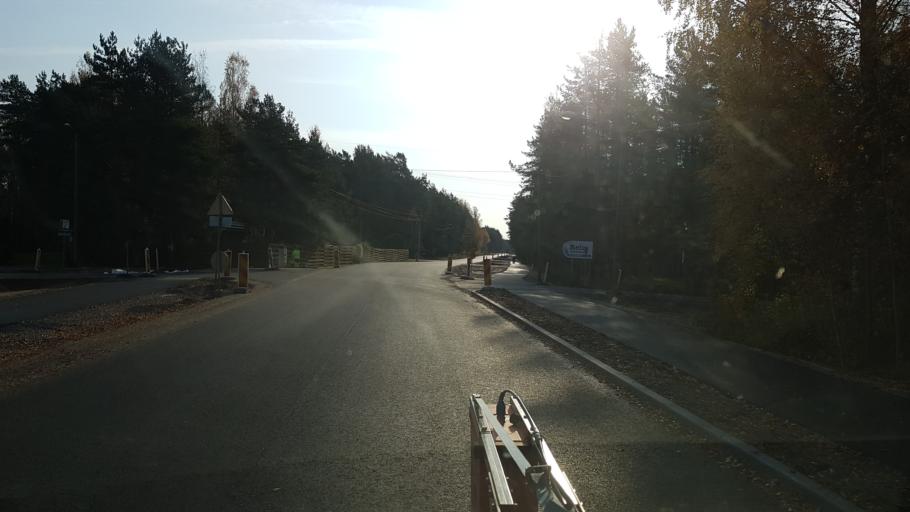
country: EE
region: Paernumaa
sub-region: Paikuse vald
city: Paikuse
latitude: 58.3622
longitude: 24.6068
